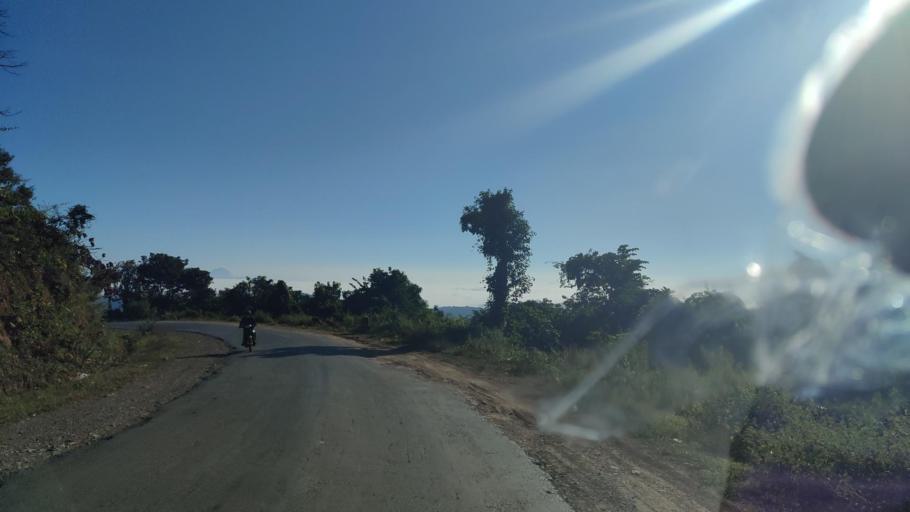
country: MM
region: Shan
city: Taunggyi
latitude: 20.9239
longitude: 97.6054
